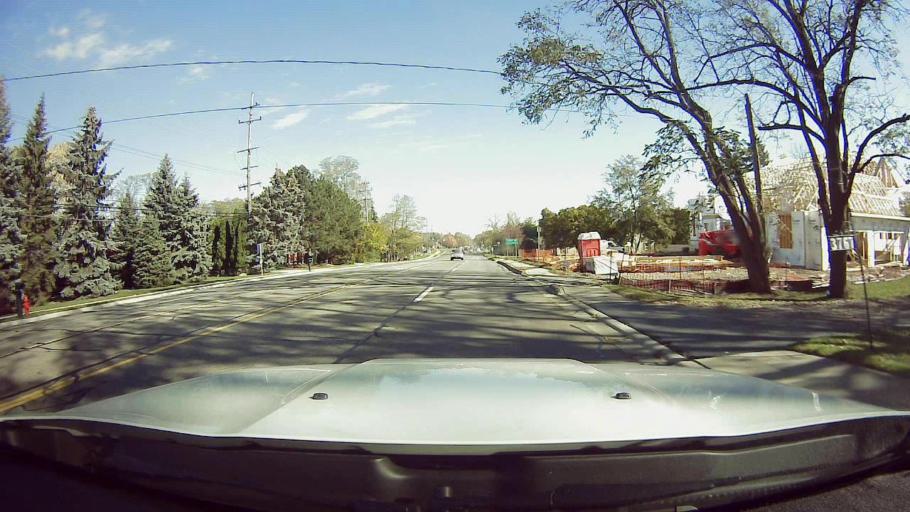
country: US
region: Michigan
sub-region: Oakland County
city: Bingham Farms
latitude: 42.5451
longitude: -83.2669
